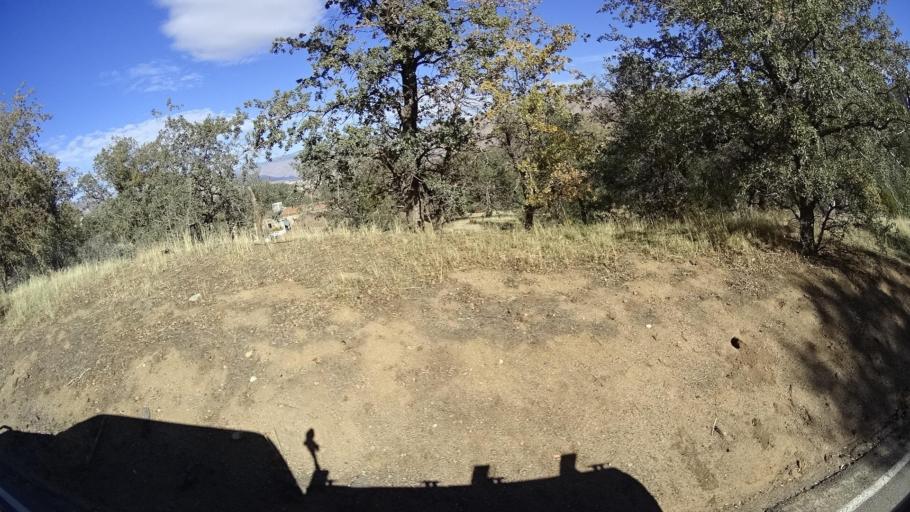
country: US
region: California
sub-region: Kern County
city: Bodfish
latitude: 35.5853
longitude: -118.4992
